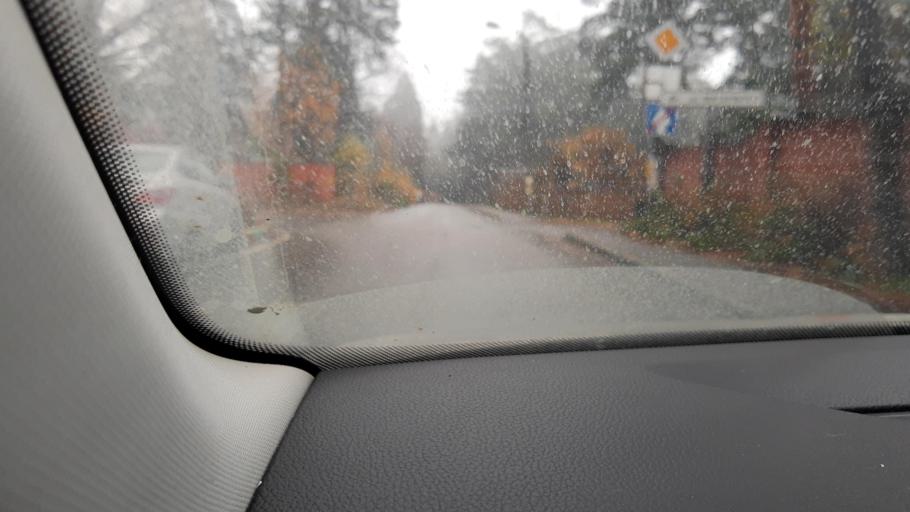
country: RU
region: Moskovskaya
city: Vidnoye
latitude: 55.5433
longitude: 37.6798
